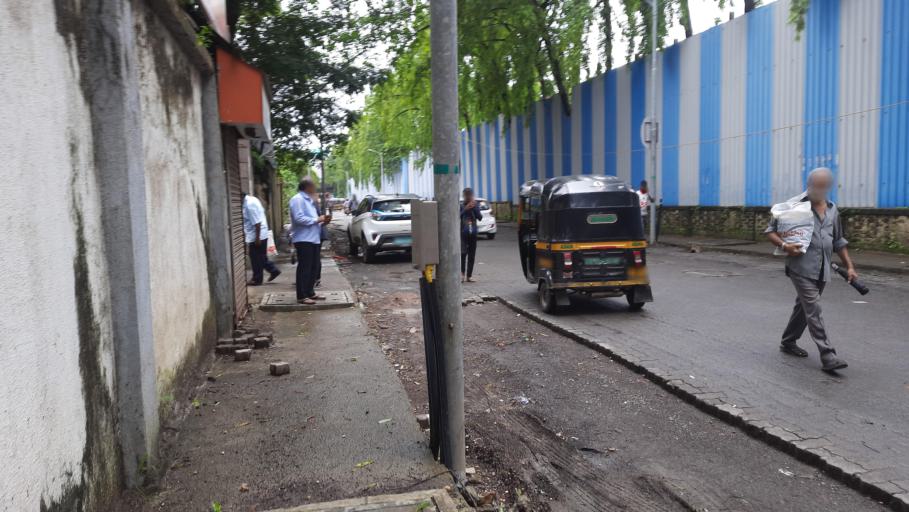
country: IN
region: Maharashtra
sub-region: Mumbai Suburban
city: Mumbai
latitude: 19.1143
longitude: 72.8446
